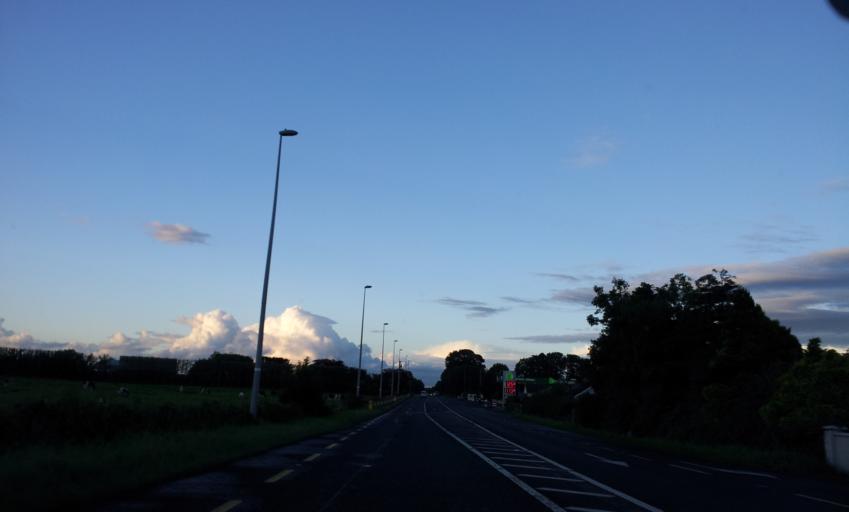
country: IE
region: Munster
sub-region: County Limerick
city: Newcastle West
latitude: 52.4785
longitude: -9.0139
